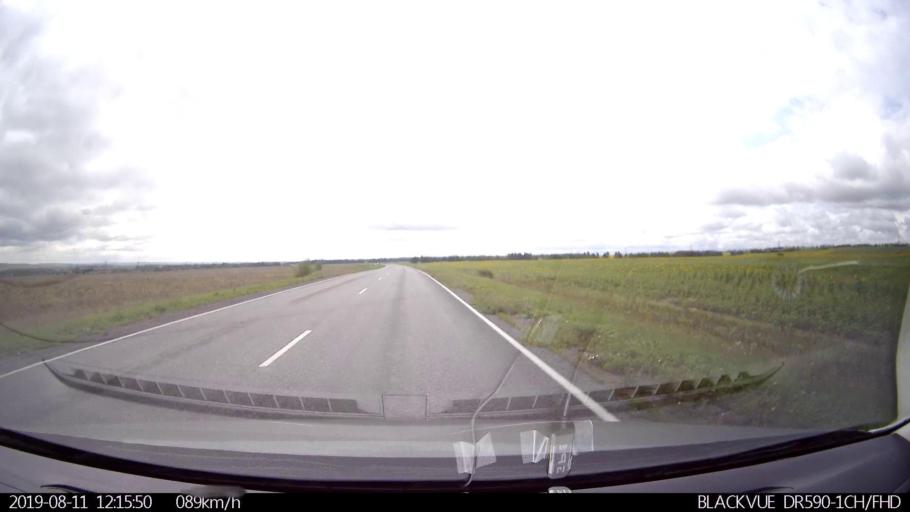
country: RU
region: Ulyanovsk
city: Ignatovka
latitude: 53.9372
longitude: 47.9645
